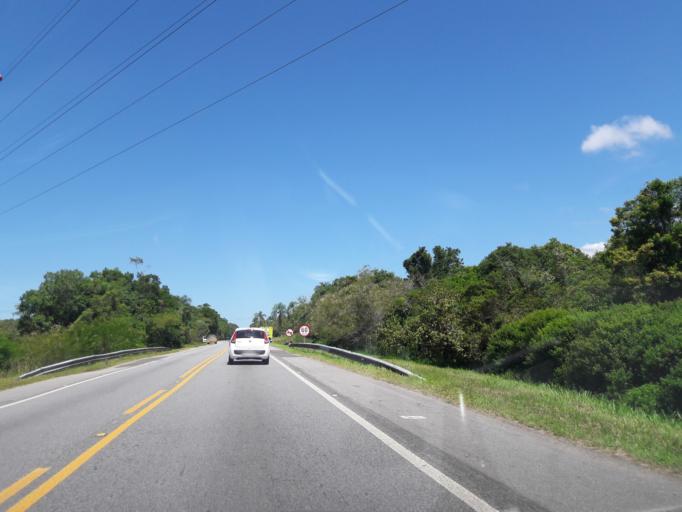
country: BR
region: Parana
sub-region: Pontal Do Parana
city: Pontal do Parana
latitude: -25.6149
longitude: -48.5491
